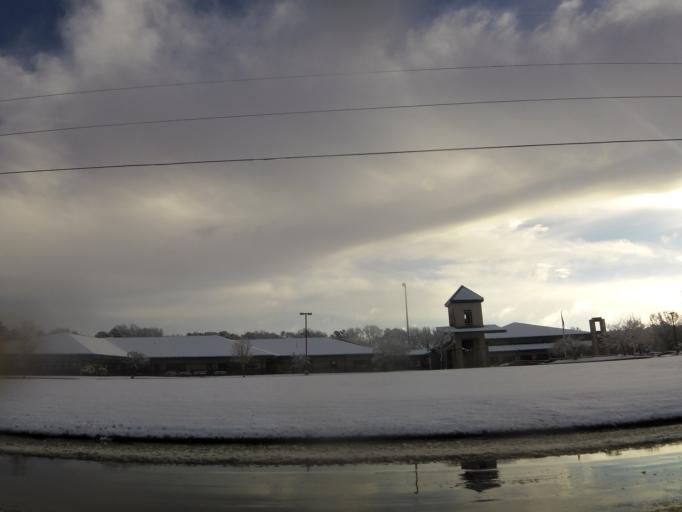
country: US
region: North Carolina
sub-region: Nash County
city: Rocky Mount
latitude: 35.9509
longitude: -77.8479
